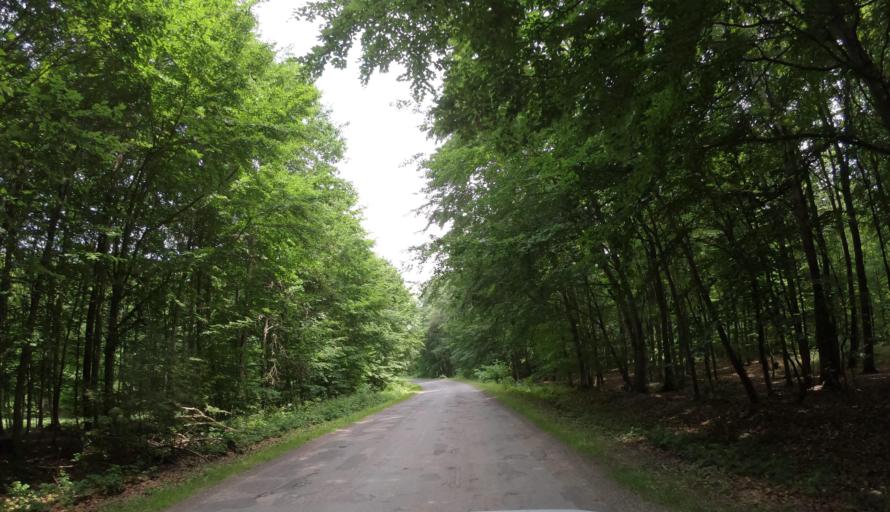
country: PL
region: West Pomeranian Voivodeship
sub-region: Powiat pyrzycki
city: Kozielice
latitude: 53.0687
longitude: 14.8002
